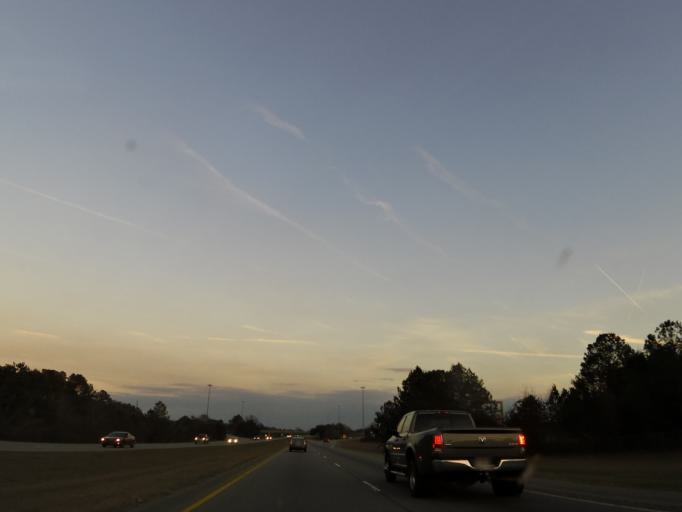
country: US
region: Georgia
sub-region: Dougherty County
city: Albany
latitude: 31.5934
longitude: -84.1307
